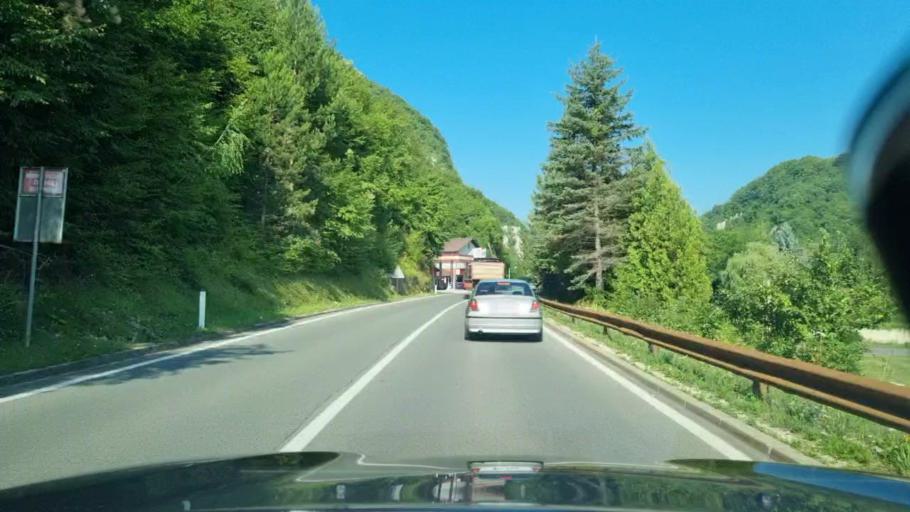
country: BA
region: Federation of Bosnia and Herzegovina
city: Jajce
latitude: 44.3443
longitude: 17.2516
